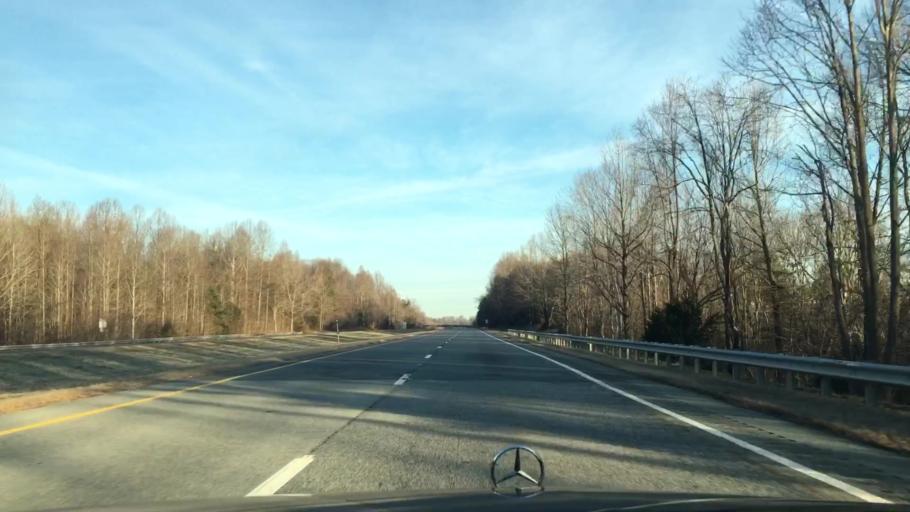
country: US
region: North Carolina
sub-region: Guilford County
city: Pleasant Garden
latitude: 36.0061
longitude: -79.7575
